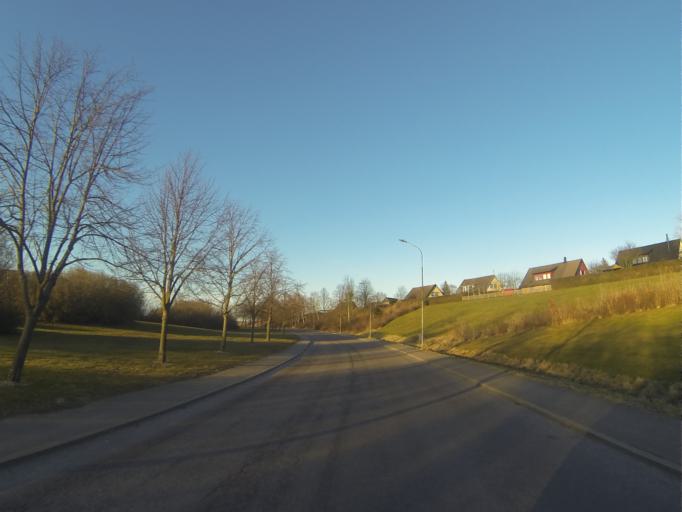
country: SE
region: Skane
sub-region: Staffanstorps Kommun
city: Staffanstorp
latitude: 55.5860
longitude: 13.1827
